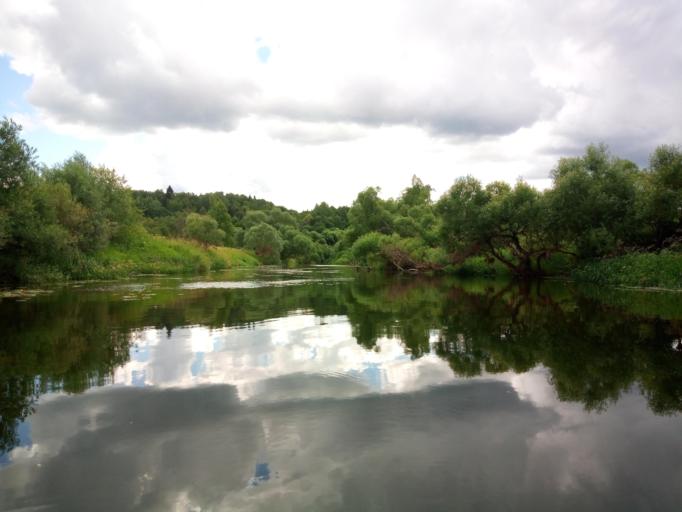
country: RU
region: Kaluga
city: Borovsk
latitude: 55.2079
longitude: 36.3569
